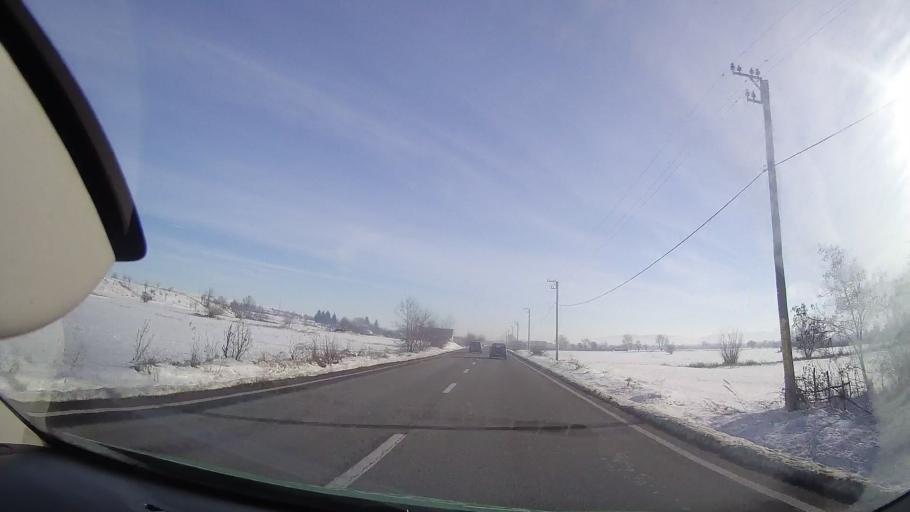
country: RO
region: Neamt
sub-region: Comuna Ghindaoani
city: Ghindaoani
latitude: 47.0819
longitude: 26.3422
